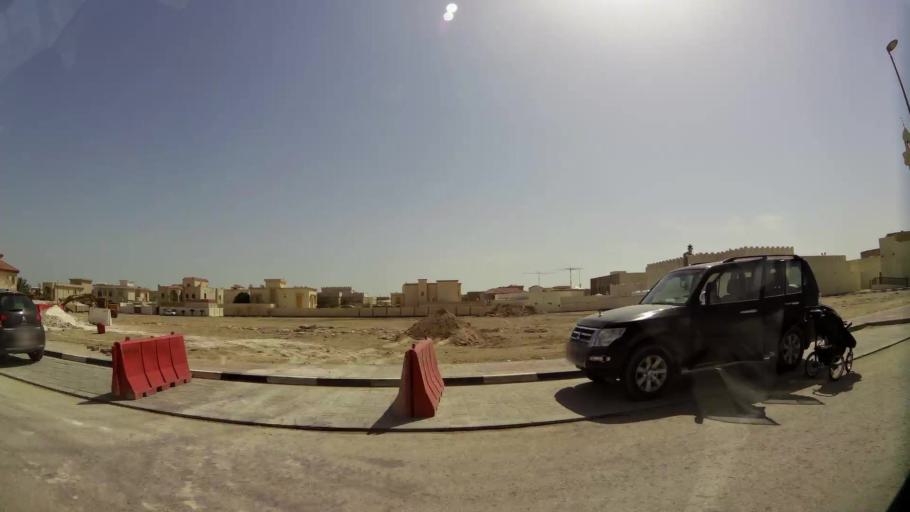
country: QA
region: Baladiyat ad Dawhah
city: Doha
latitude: 25.3575
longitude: 51.4969
